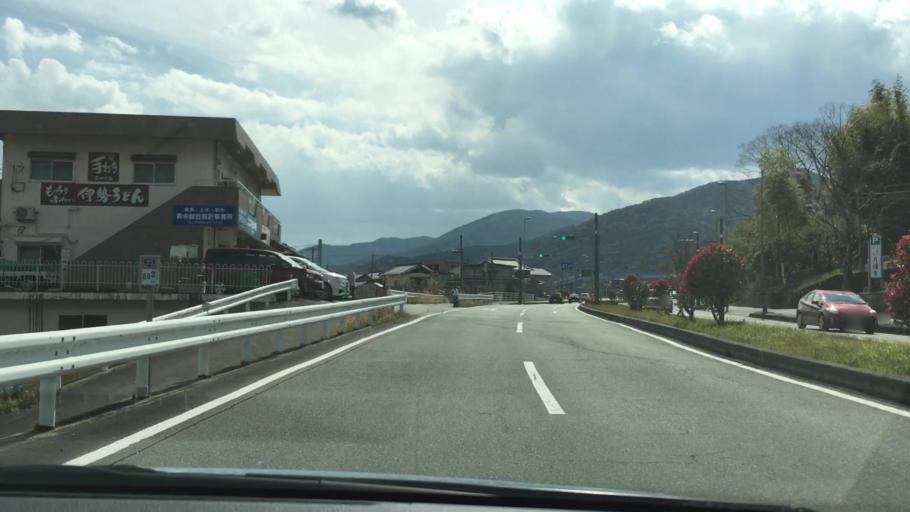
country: JP
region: Mie
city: Ise
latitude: 34.4722
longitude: 136.7294
